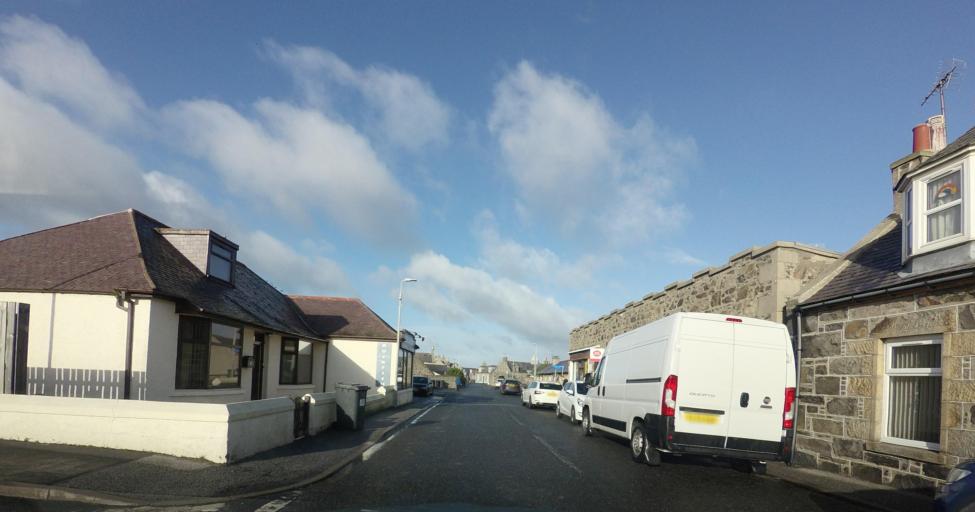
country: GB
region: Scotland
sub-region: Aberdeenshire
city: Whitehills
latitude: 57.6768
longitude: -2.5784
